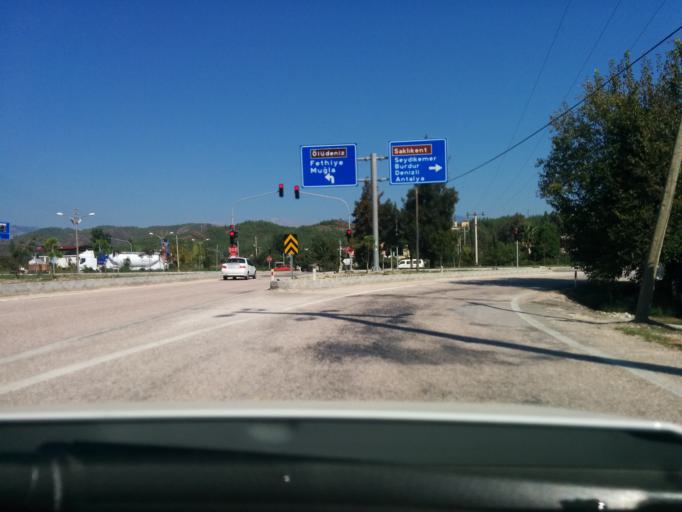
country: TR
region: Mugla
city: Kemer
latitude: 36.6327
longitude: 29.3555
